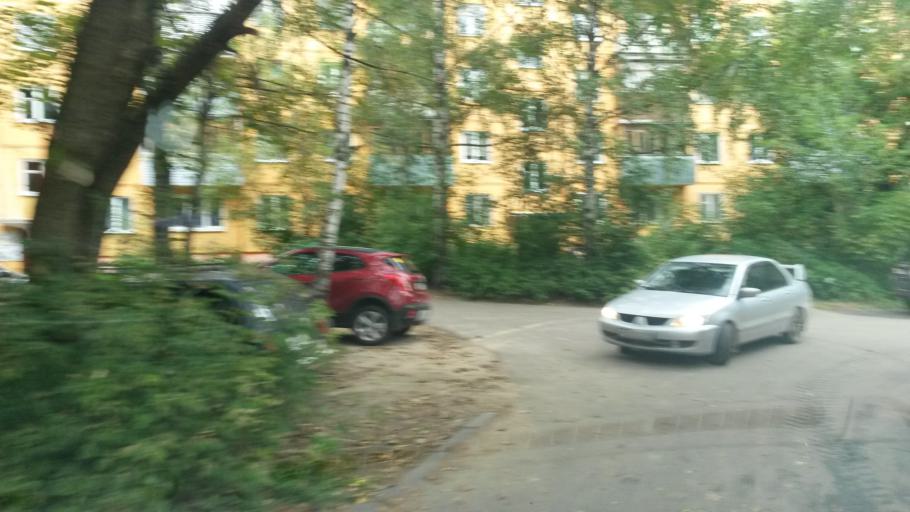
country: RU
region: Ivanovo
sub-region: Gorod Ivanovo
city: Ivanovo
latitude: 57.0178
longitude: 40.9626
